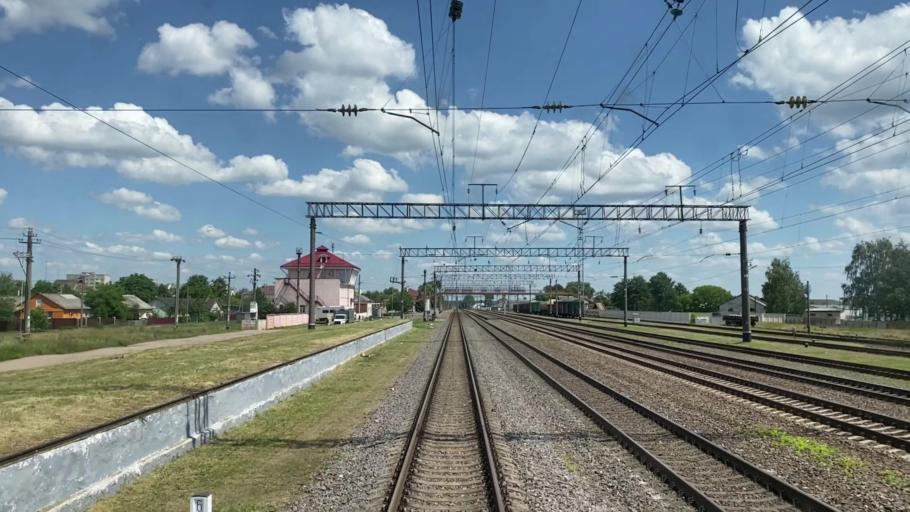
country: BY
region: Brest
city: Ivatsevichy
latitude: 52.7074
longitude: 25.3409
